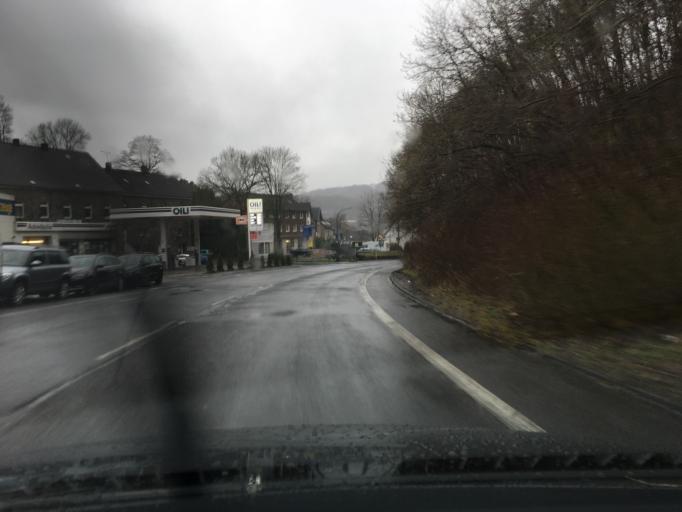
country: DE
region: North Rhine-Westphalia
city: Hattingen
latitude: 51.3745
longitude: 7.1434
